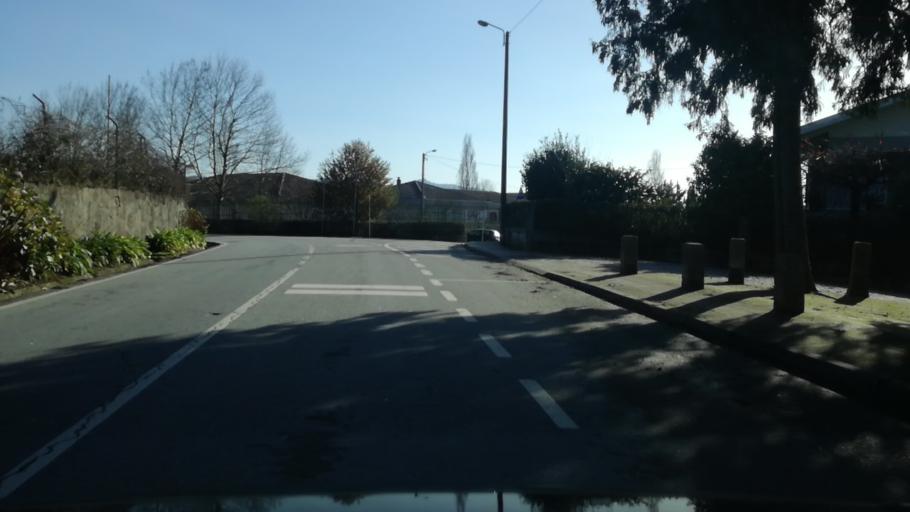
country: PT
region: Braga
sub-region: Guimaraes
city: Ponte
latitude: 41.5189
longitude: -8.3199
